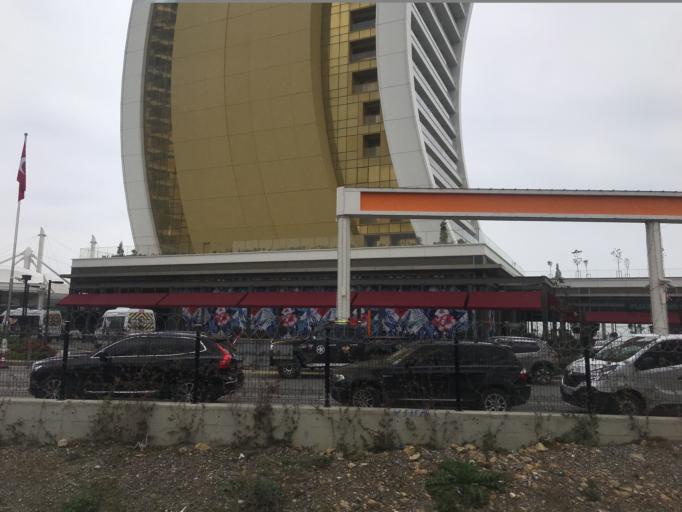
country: TR
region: Istanbul
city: Pendik
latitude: 40.8850
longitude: 29.2046
